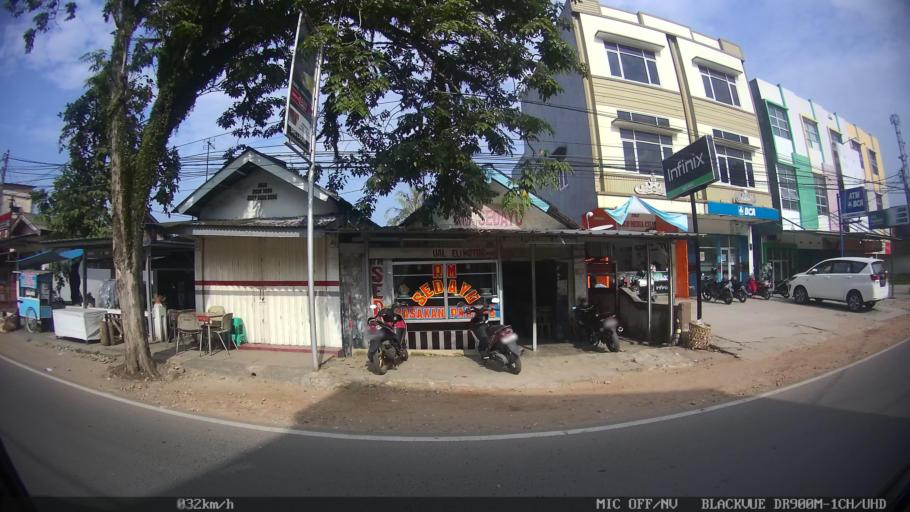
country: ID
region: Lampung
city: Panjang
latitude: -5.4703
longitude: 105.3225
